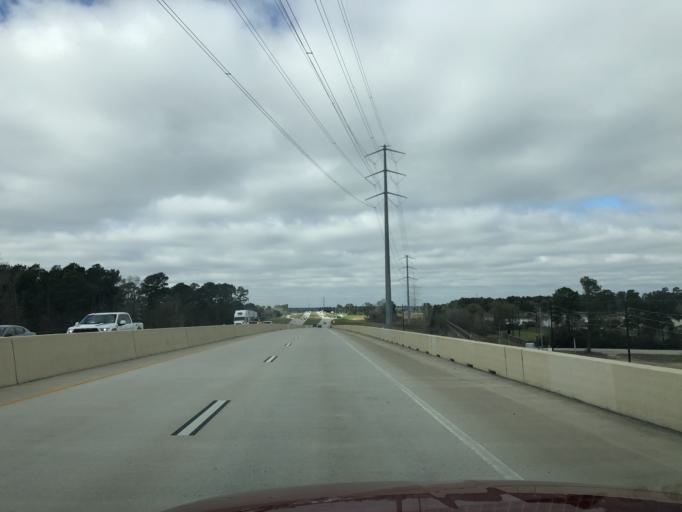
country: US
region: Texas
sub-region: Montgomery County
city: The Woodlands
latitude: 30.0944
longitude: -95.4944
